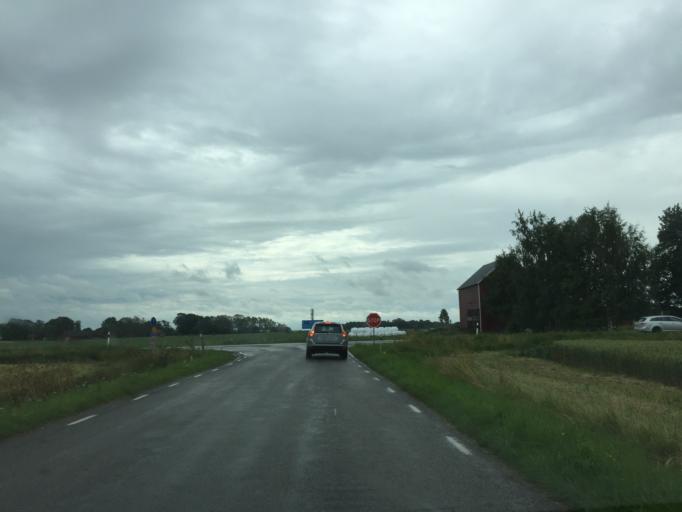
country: SE
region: OEstergoetland
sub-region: Vadstena Kommun
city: Vadstena
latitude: 58.4314
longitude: 14.8559
